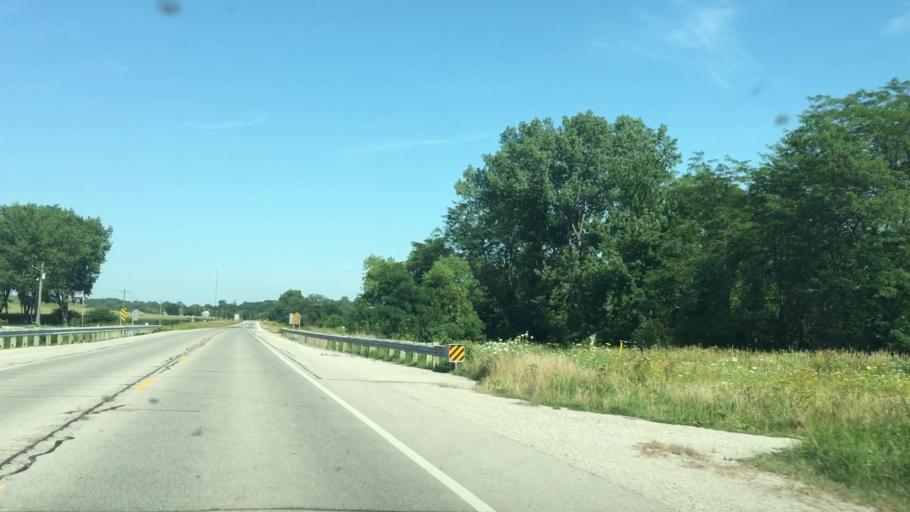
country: US
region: Iowa
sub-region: Johnson County
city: Tiffin
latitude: 41.7144
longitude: -91.7122
